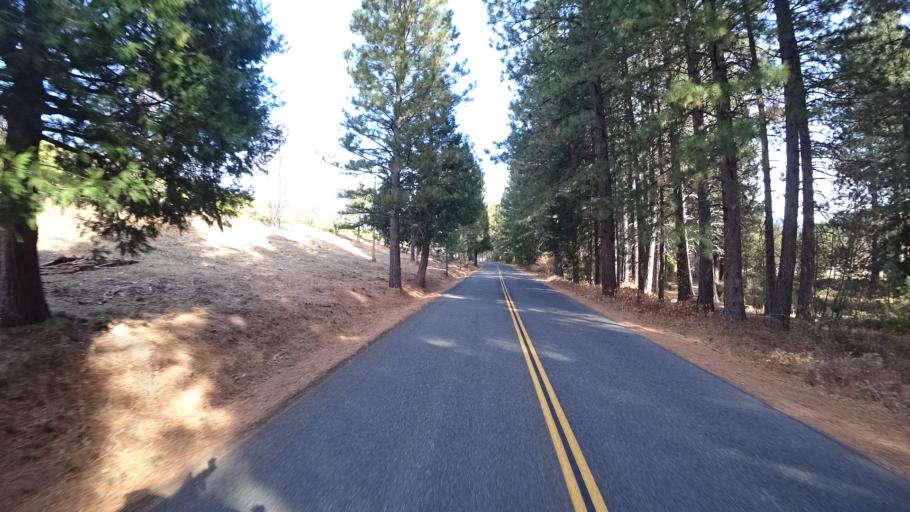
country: US
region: California
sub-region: Siskiyou County
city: Weed
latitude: 41.4138
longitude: -122.3934
